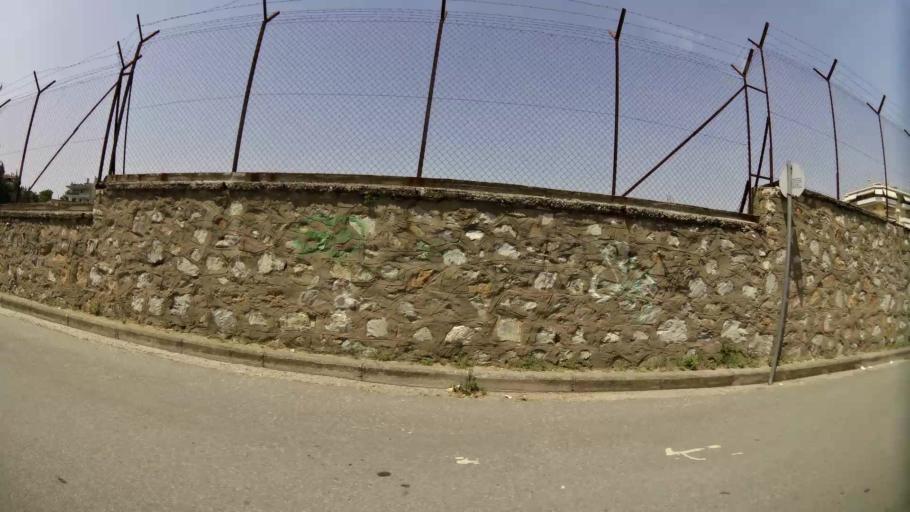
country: GR
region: Central Macedonia
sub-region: Nomos Thessalonikis
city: Evosmos
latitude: 40.6722
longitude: 22.9029
